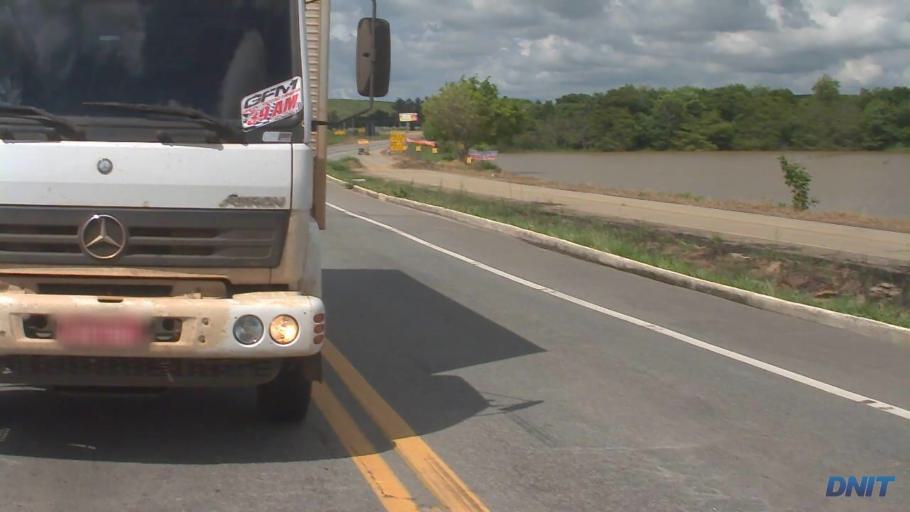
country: BR
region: Minas Gerais
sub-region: Governador Valadares
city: Governador Valadares
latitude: -19.0488
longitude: -42.1563
